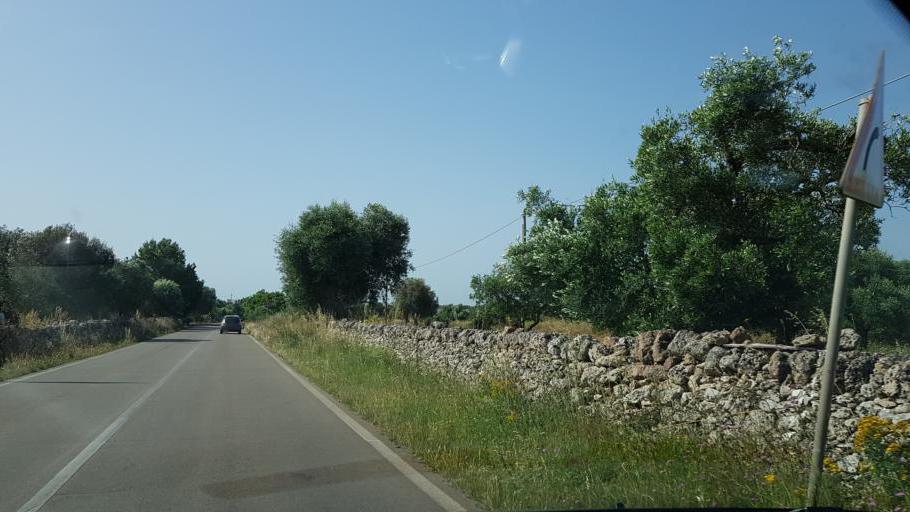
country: IT
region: Apulia
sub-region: Provincia di Lecce
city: Porto Cesareo
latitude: 40.3127
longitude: 17.8625
